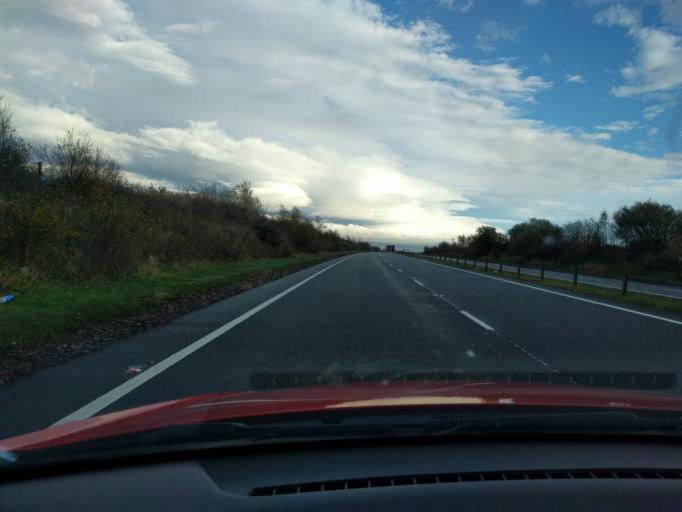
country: GB
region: Scotland
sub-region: East Lothian
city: Dunbar
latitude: 55.9888
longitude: -2.5753
